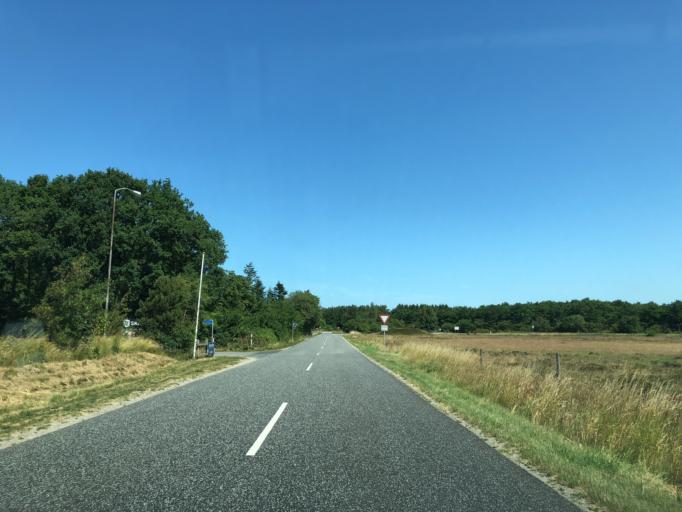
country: DK
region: Central Jutland
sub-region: Skive Kommune
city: Skive
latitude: 56.5298
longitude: 9.0361
